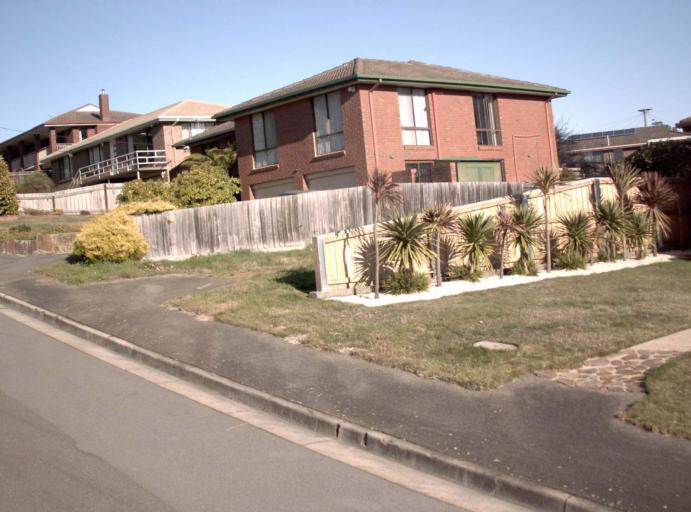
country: AU
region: Tasmania
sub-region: Launceston
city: Summerhill
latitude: -41.4661
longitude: 147.1242
